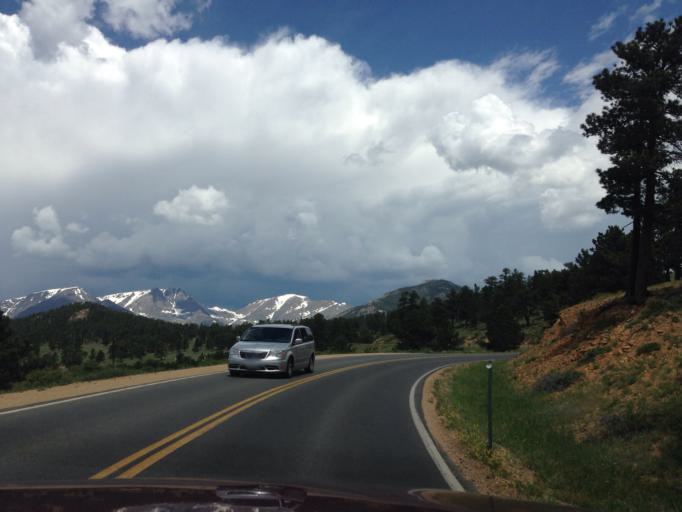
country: US
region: Colorado
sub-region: Larimer County
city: Estes Park
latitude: 40.3811
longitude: -105.6048
